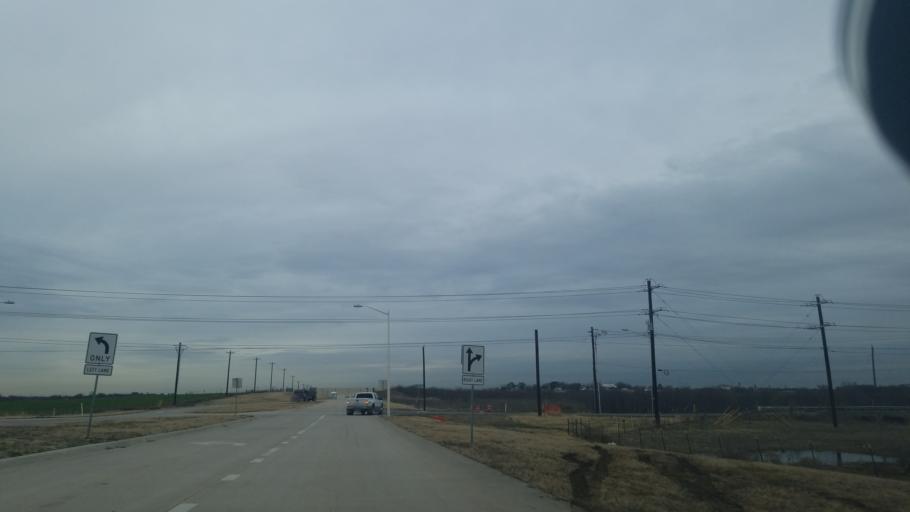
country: US
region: Texas
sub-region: Denton County
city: Denton
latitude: 33.2185
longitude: -97.1860
